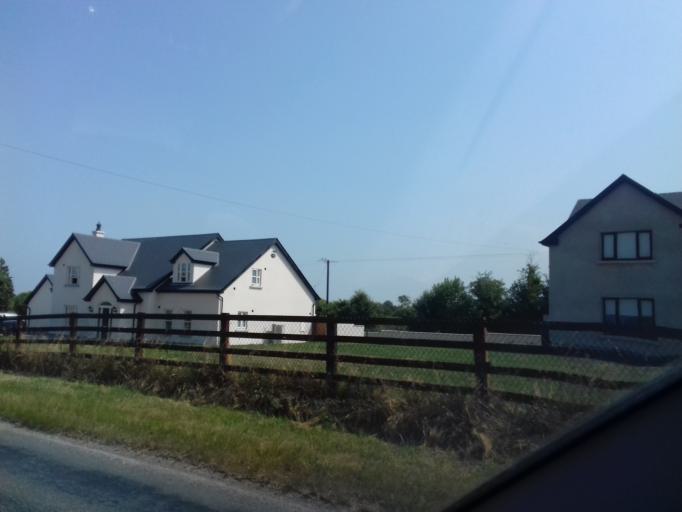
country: IE
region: Leinster
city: Balrothery
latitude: 53.5972
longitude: -6.2293
